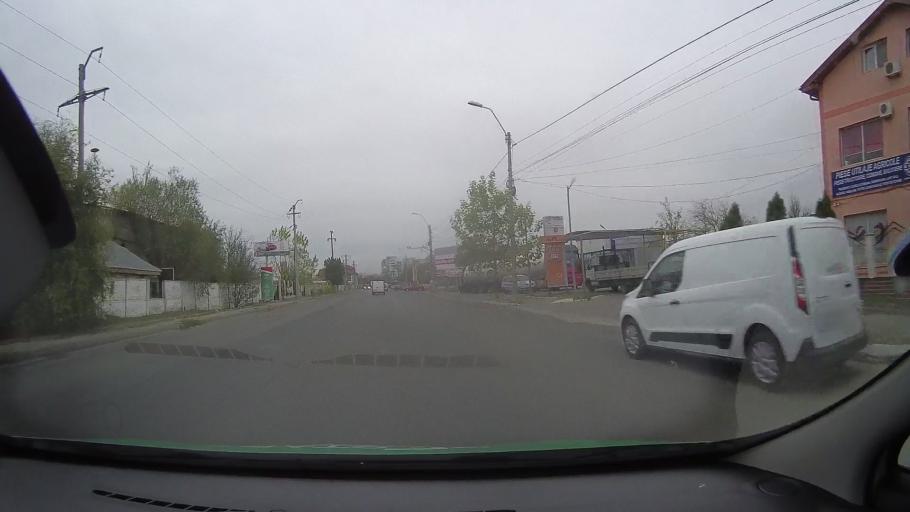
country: RO
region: Ialomita
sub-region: Comuna Slobozia
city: Slobozia
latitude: 44.5725
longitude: 27.3855
